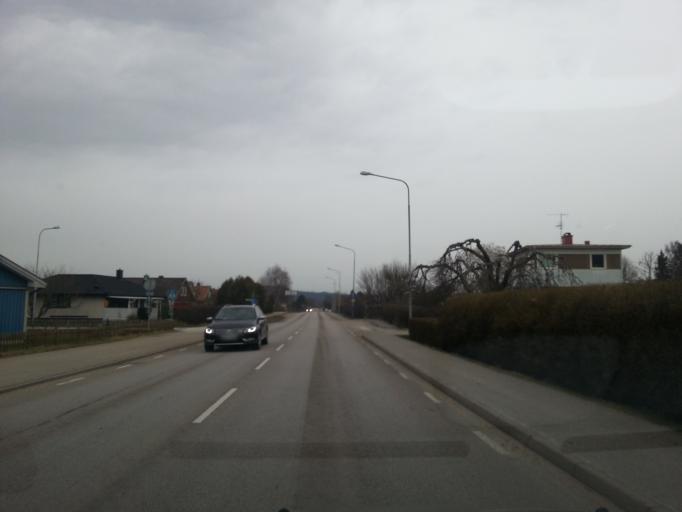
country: SE
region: Vaestra Goetaland
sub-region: Lilla Edets Kommun
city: Lilla Edet
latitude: 58.1272
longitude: 12.1338
